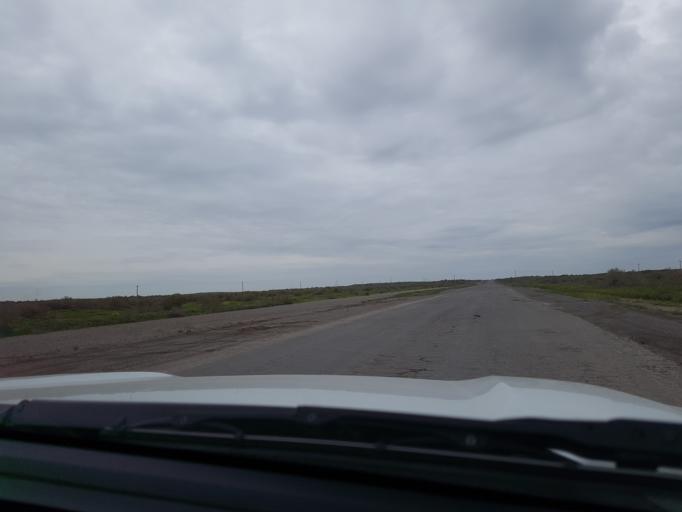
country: TM
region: Mary
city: Bayramaly
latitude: 37.9223
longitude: 62.6241
